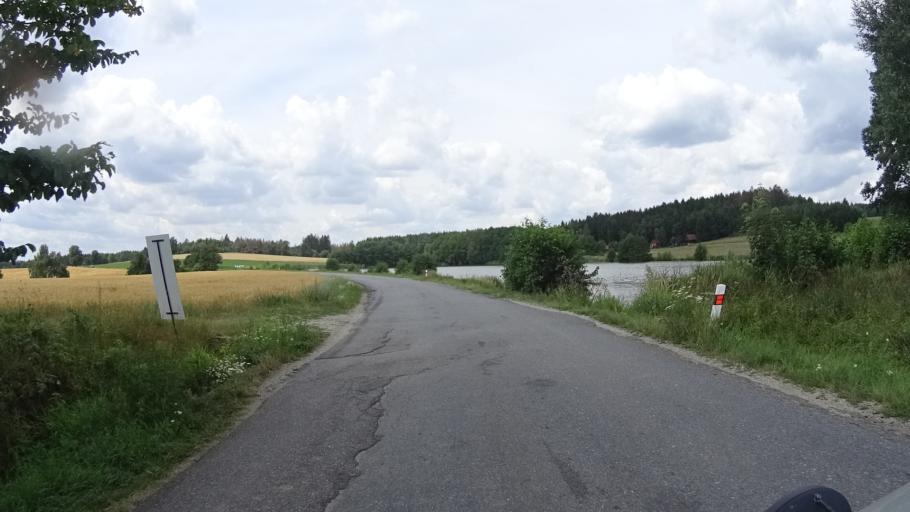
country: CZ
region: Vysocina
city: Merin
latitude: 49.4114
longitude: 15.9409
